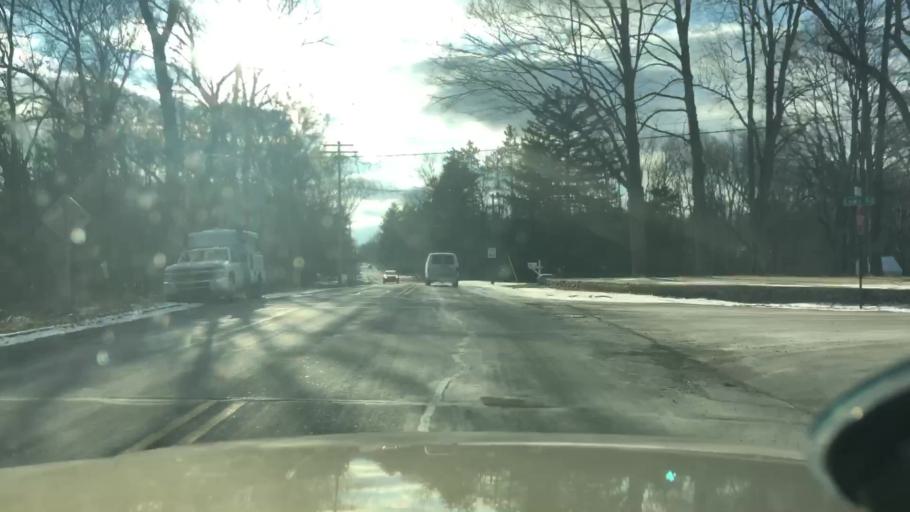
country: US
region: Michigan
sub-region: Jackson County
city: Vandercook Lake
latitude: 42.1984
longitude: -84.4423
